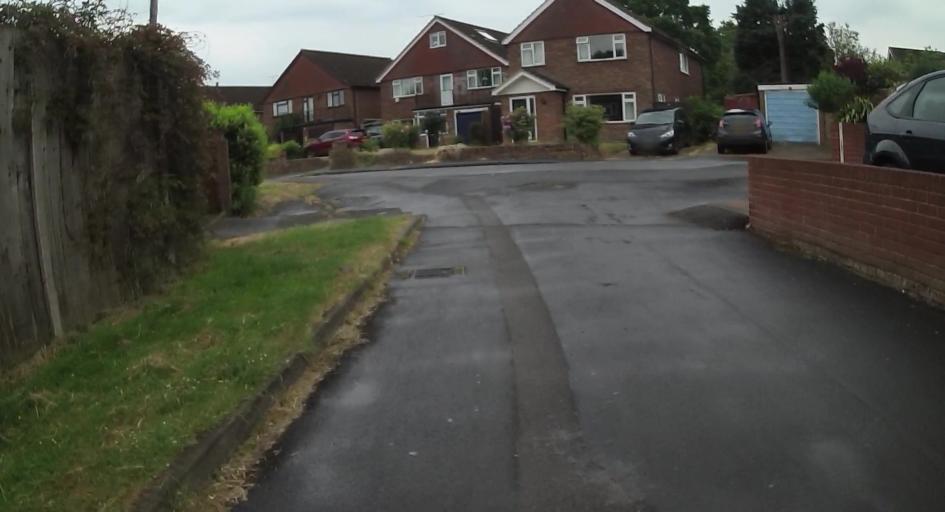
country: GB
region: England
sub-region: Hampshire
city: Farnborough
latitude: 51.2954
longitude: -0.7688
